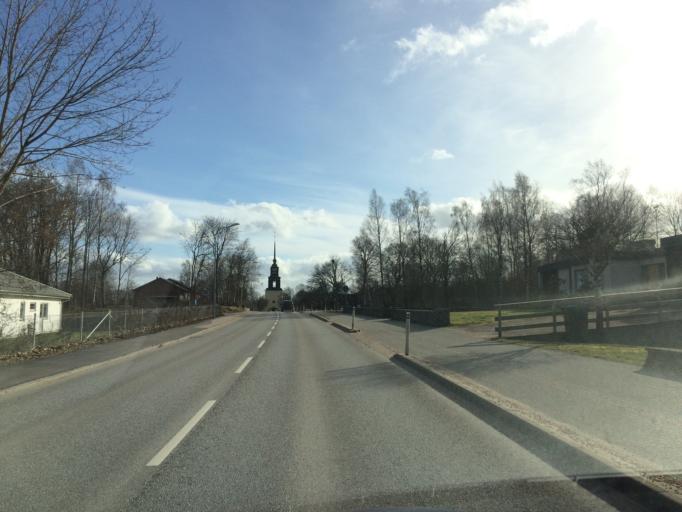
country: SE
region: Kronoberg
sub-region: Almhults Kommun
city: AElmhult
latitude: 56.5564
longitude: 14.1295
